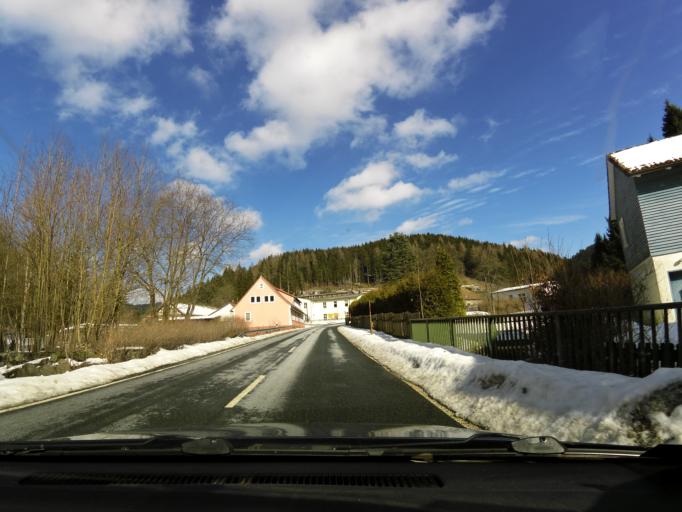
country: DE
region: Lower Saxony
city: Sankt Andreasberg
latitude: 51.6945
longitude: 10.5026
